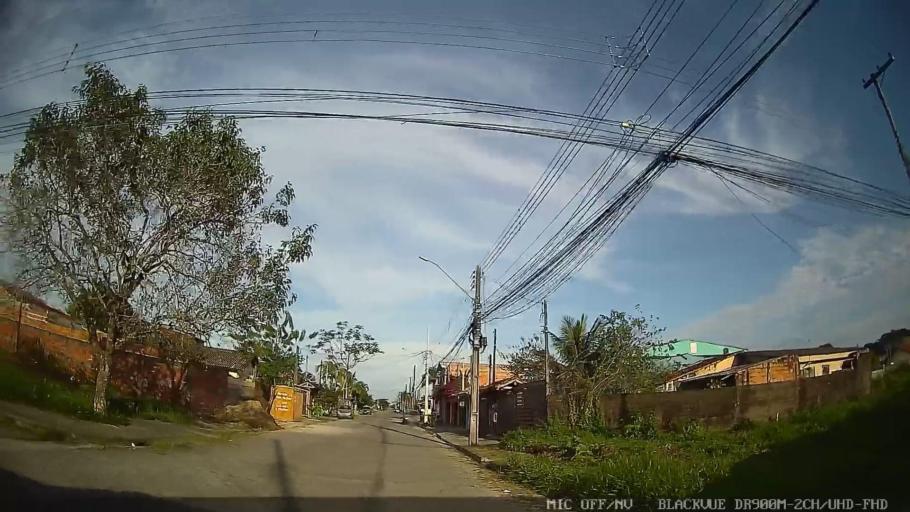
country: BR
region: Sao Paulo
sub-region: Itanhaem
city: Itanhaem
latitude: -24.1561
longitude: -46.7754
